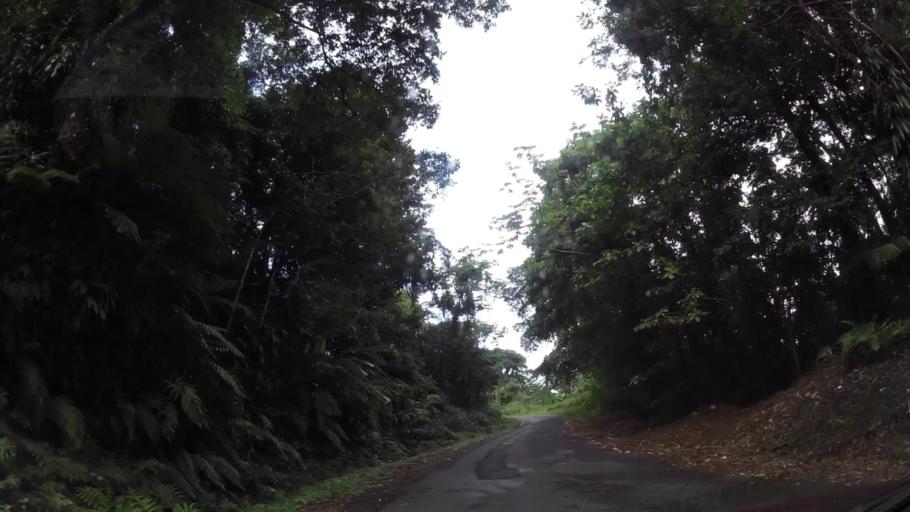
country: DM
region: Saint Paul
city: Pont Casse
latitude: 15.4000
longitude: -61.3104
